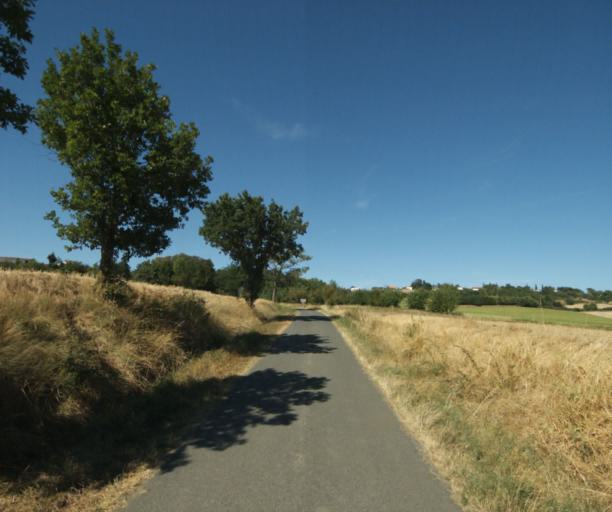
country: FR
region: Midi-Pyrenees
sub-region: Departement de la Haute-Garonne
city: Saint-Felix-Lauragais
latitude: 43.5142
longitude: 1.9106
